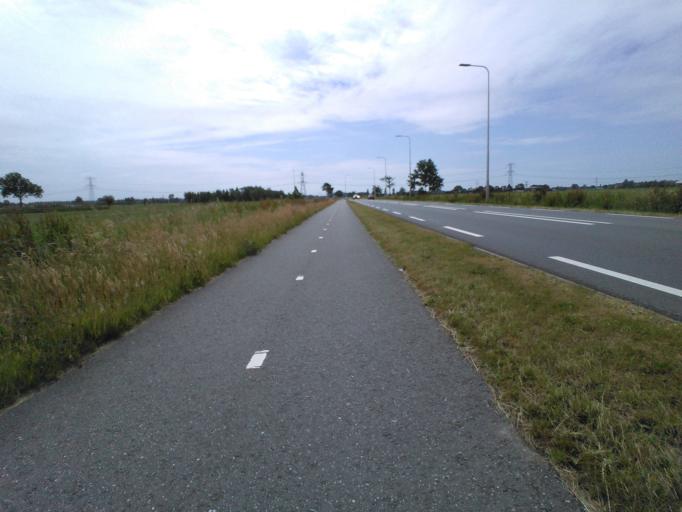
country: NL
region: South Holland
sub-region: Molenwaard
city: Nieuw-Lekkerland
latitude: 51.8756
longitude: 4.7391
